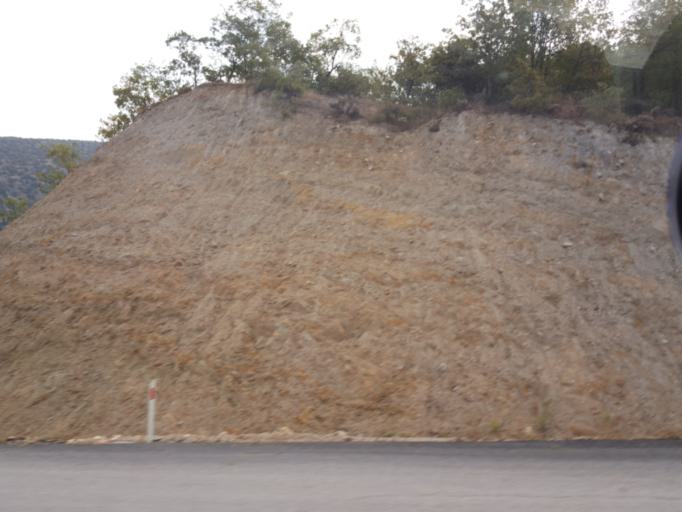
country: TR
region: Amasya
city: Gediksaray
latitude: 40.4601
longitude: 35.7760
